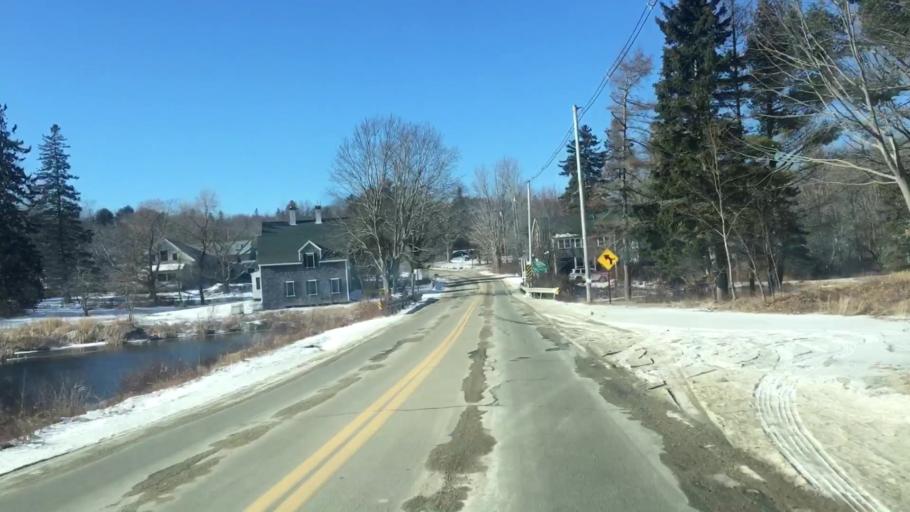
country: US
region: Maine
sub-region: Hancock County
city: Sedgwick
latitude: 44.3461
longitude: -68.6825
